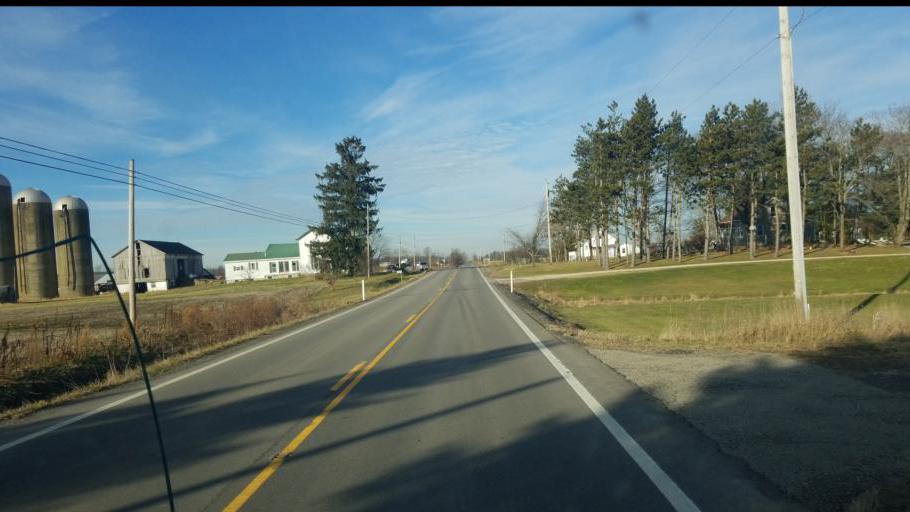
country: US
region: Ohio
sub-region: Ashtabula County
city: Andover
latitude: 41.5389
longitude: -80.6662
